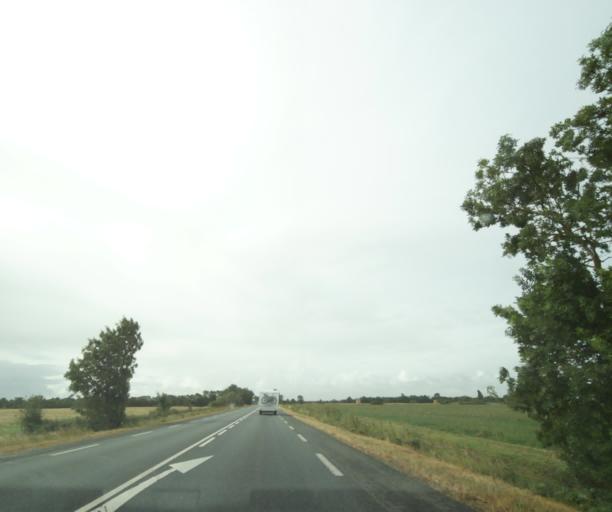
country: FR
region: Pays de la Loire
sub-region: Departement de la Vendee
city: Sainte-Gemme-la-Plaine
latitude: 46.4372
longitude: -1.0998
